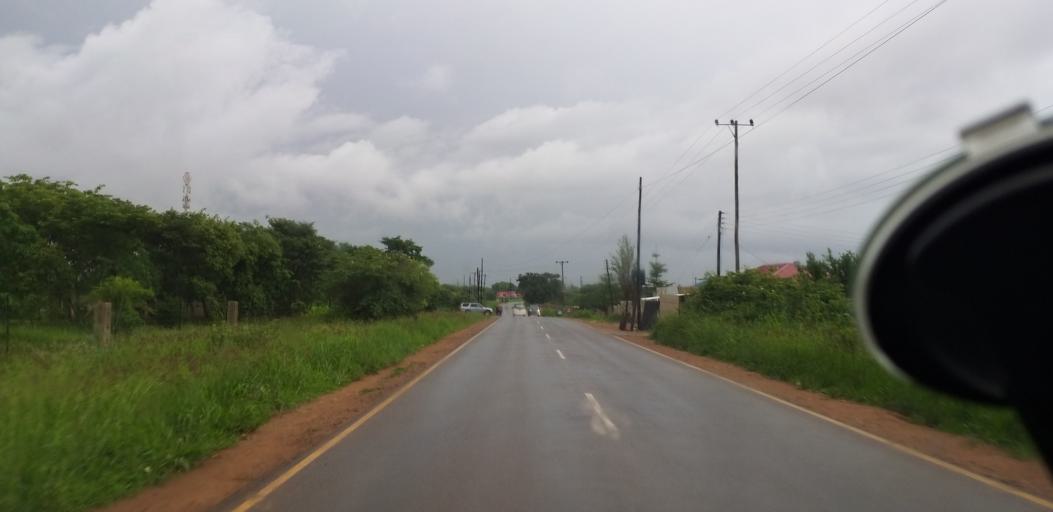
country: ZM
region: Lusaka
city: Lusaka
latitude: -15.4919
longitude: 28.3137
